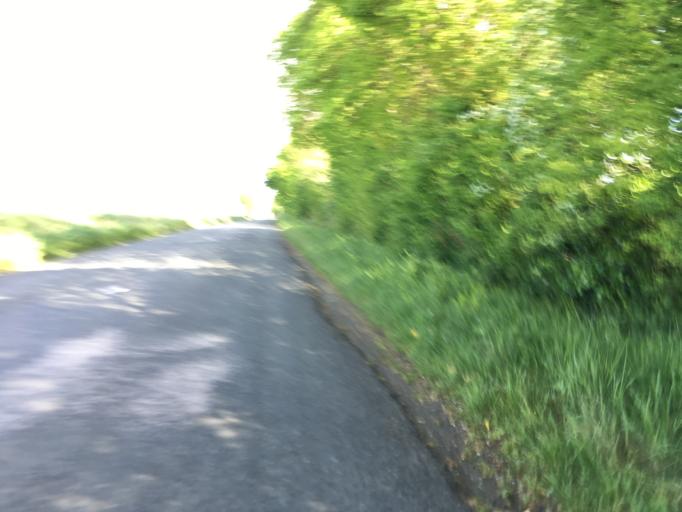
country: FR
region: Poitou-Charentes
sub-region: Departement de la Charente-Maritime
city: Verines
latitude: 46.1737
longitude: -0.9059
